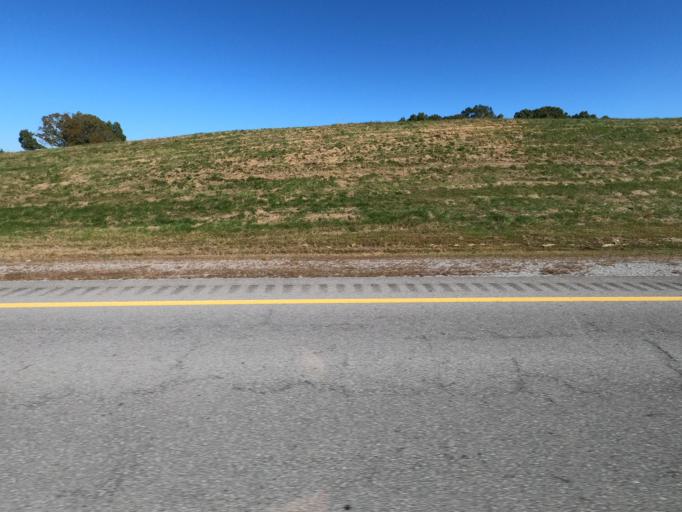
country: US
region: Tennessee
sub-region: Williamson County
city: Fairview
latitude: 35.8920
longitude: -87.1255
